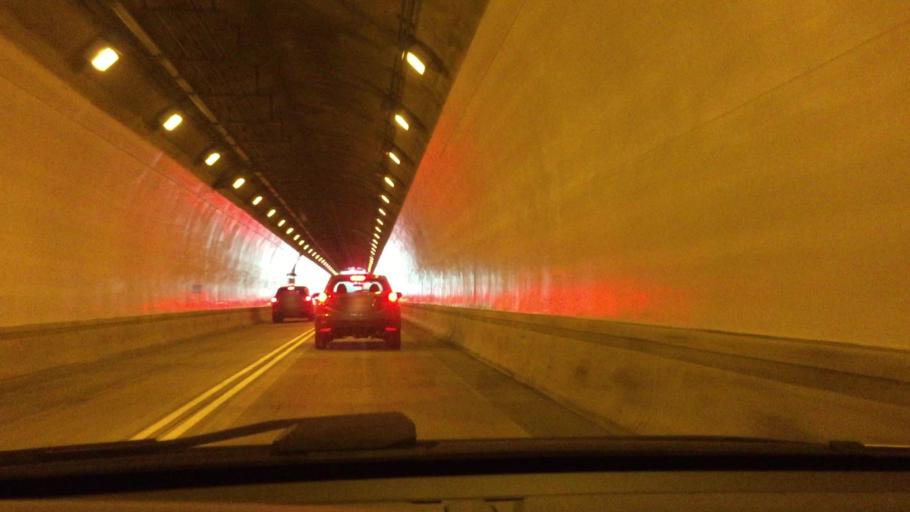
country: US
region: Pennsylvania
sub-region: Allegheny County
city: Mount Oliver
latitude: 40.4208
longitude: -80.0051
